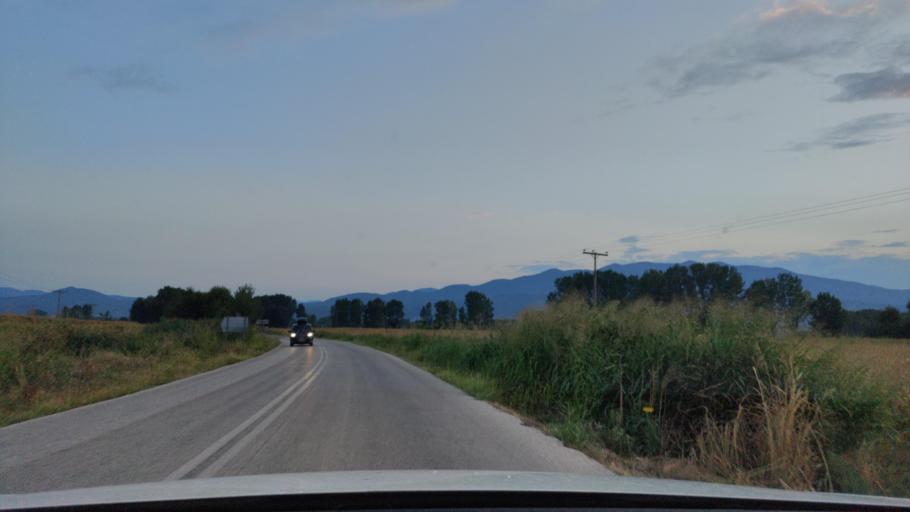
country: GR
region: Central Macedonia
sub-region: Nomos Serron
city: Chrysochorafa
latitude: 41.1657
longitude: 23.2474
